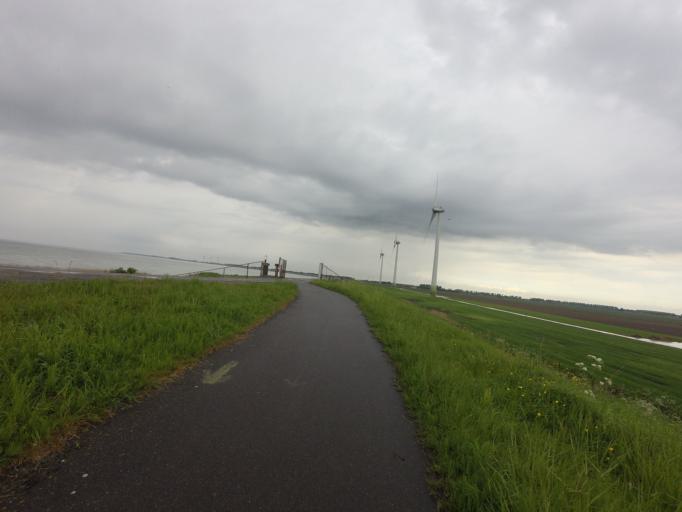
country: NL
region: South Holland
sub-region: Gemeente Goeree-Overflakkee
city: Middelharnis
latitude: 51.6885
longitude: 4.1641
